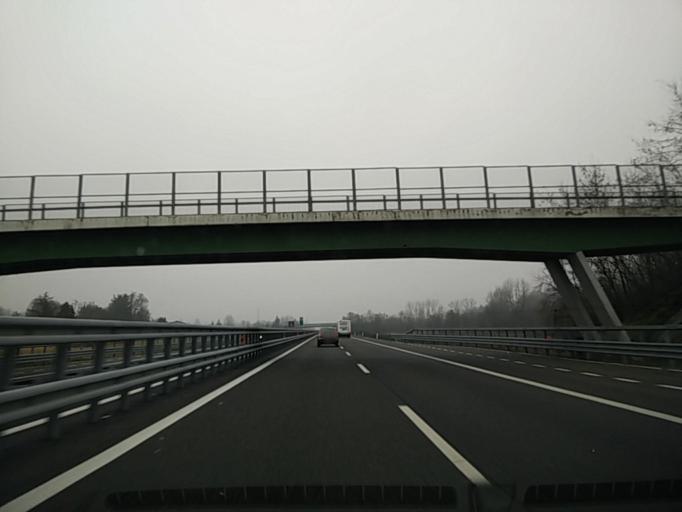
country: IT
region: Piedmont
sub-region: Provincia di Asti
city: Villafranca d'Asti
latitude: 44.9303
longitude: 8.0042
